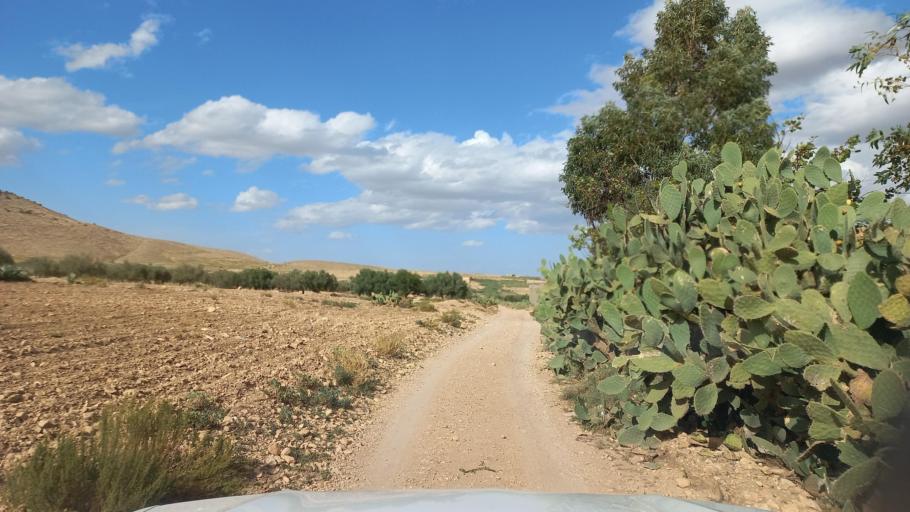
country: TN
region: Al Qasrayn
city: Sbiba
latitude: 35.4519
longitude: 9.0729
